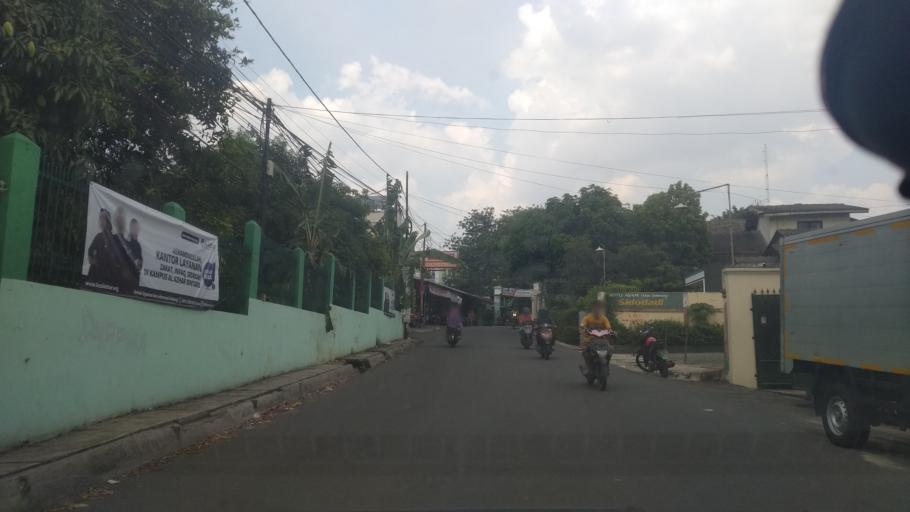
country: ID
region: Banten
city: South Tangerang
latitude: -6.2675
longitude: 106.7425
